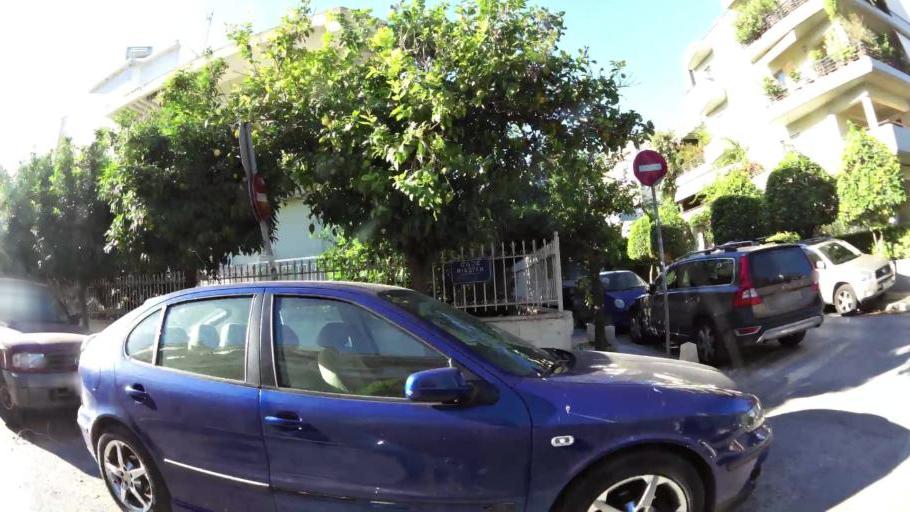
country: GR
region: Attica
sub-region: Nomarchia Athinas
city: Khalandrion
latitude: 38.0170
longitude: 23.7916
